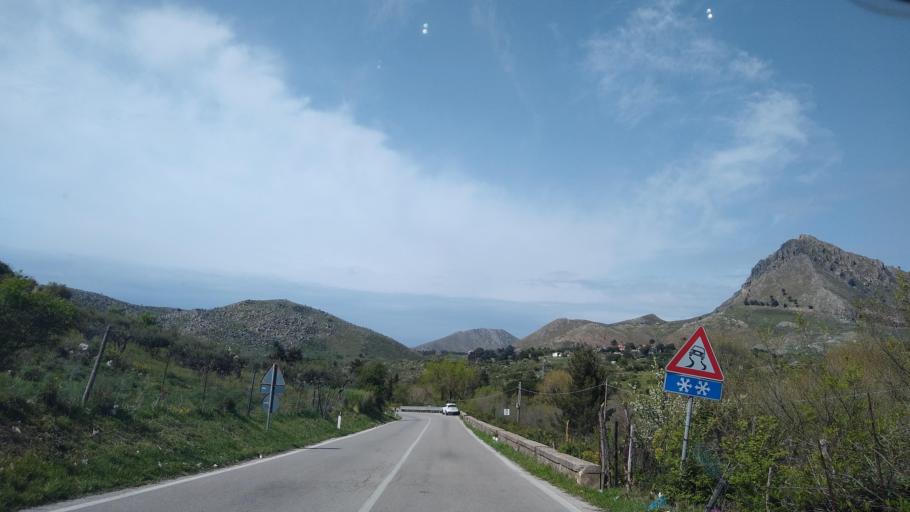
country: IT
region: Sicily
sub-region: Palermo
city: Pioppo
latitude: 38.0423
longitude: 13.1995
